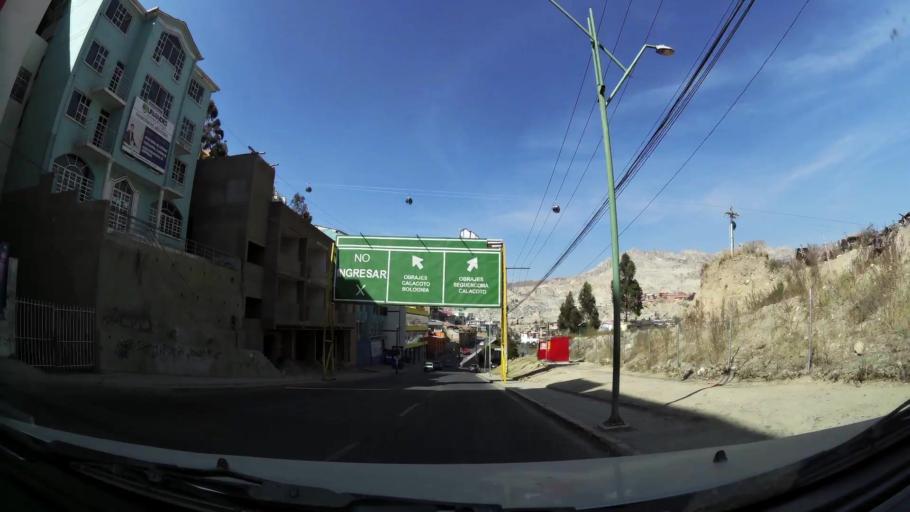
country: BO
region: La Paz
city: La Paz
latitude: -16.5185
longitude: -68.1146
